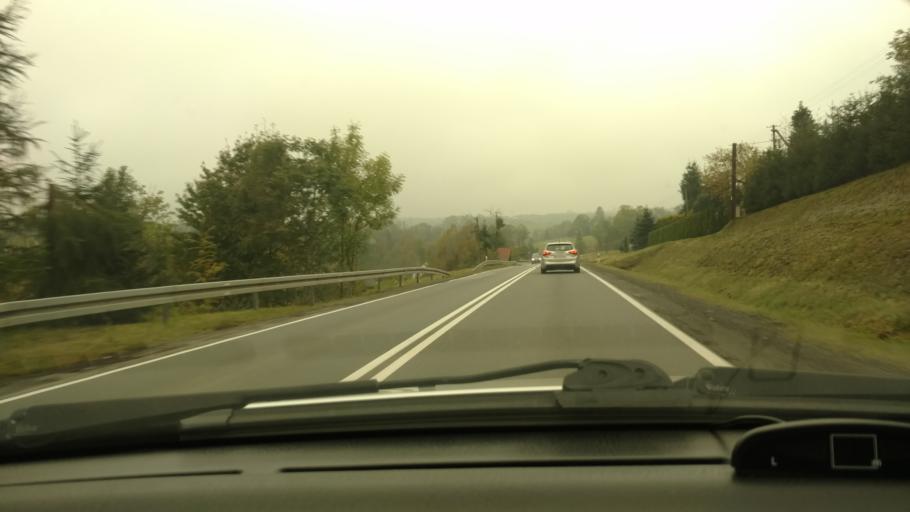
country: PL
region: Lesser Poland Voivodeship
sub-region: Powiat nowosadecki
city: Grybow
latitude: 49.6211
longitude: 20.9023
